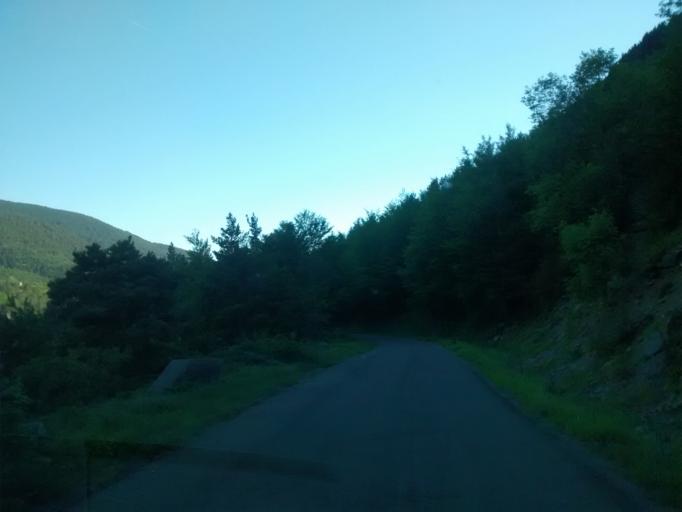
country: ES
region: Aragon
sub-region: Provincia de Huesca
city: Canfranc
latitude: 42.7333
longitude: -0.5950
